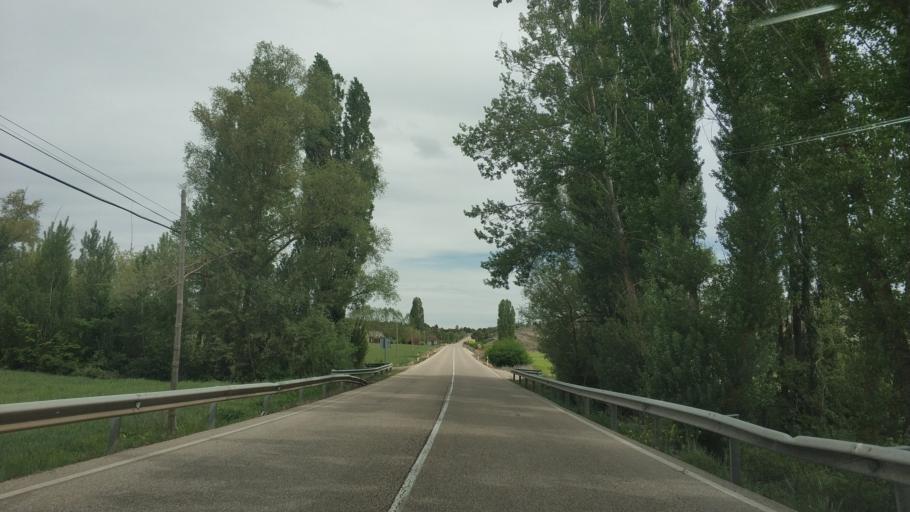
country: ES
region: Castille and Leon
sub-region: Provincia de Soria
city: El Burgo de Osma
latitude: 41.5811
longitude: -3.0396
